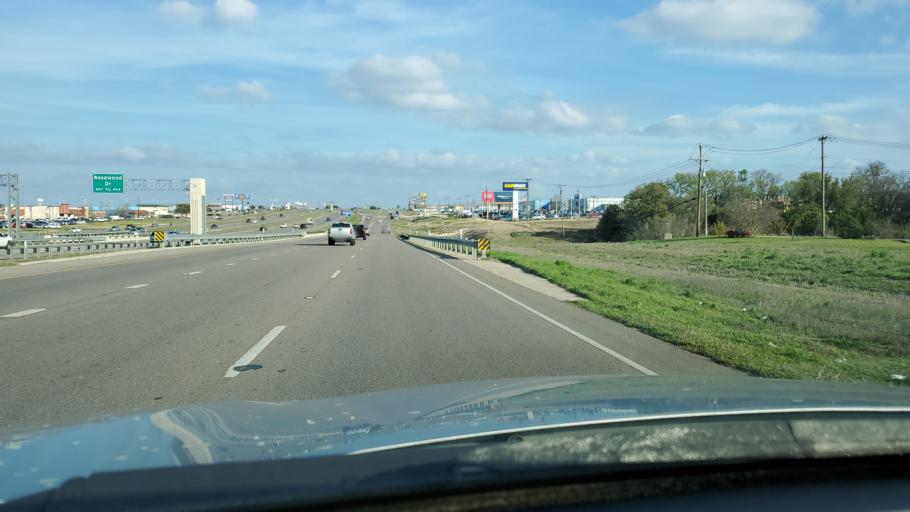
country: US
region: Texas
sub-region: Bell County
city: Killeen
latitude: 31.0849
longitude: -97.7087
